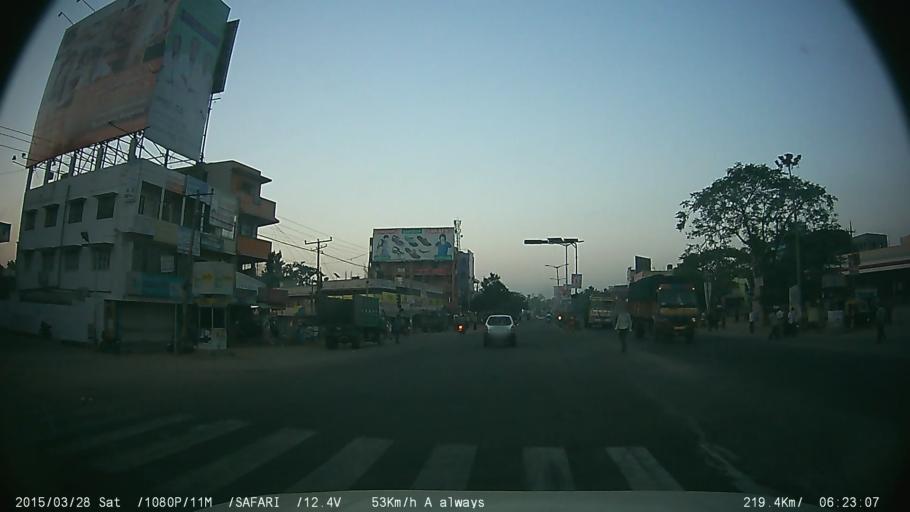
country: IN
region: Karnataka
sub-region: Ramanagara
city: Ramanagaram
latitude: 12.7231
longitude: 77.2753
